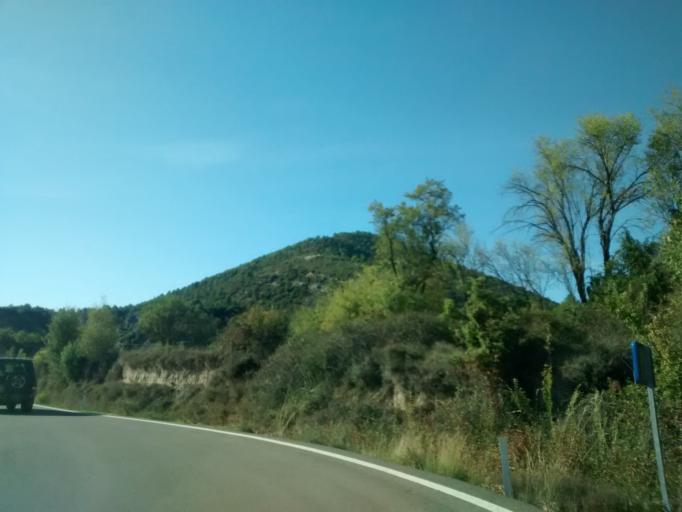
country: ES
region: Aragon
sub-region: Provincia de Huesca
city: Loarre
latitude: 42.3887
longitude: -0.7098
